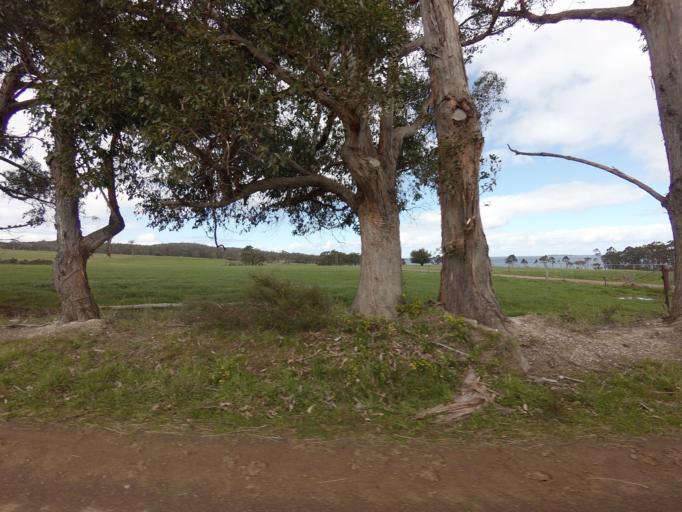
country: AU
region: Tasmania
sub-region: Huon Valley
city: Geeveston
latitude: -43.4305
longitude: 146.9911
